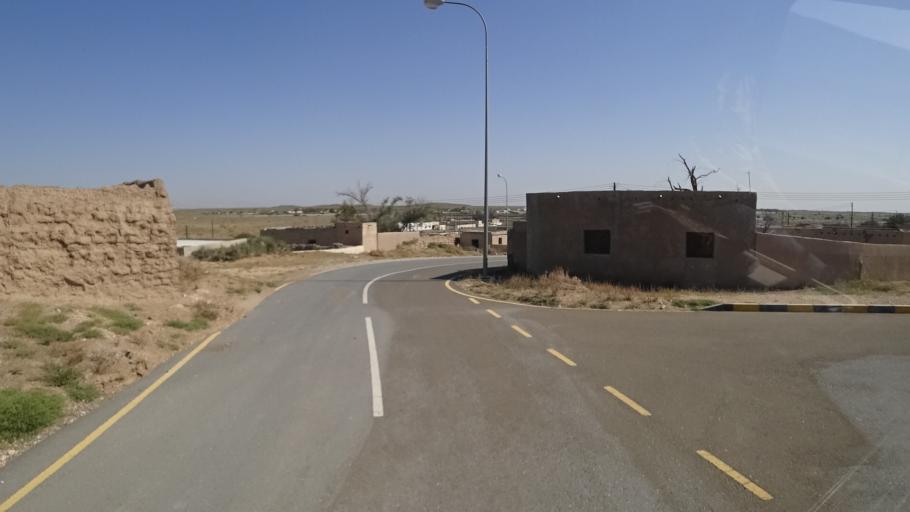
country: AE
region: Abu Dhabi
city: Al Ain
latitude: 23.9809
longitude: 55.8362
